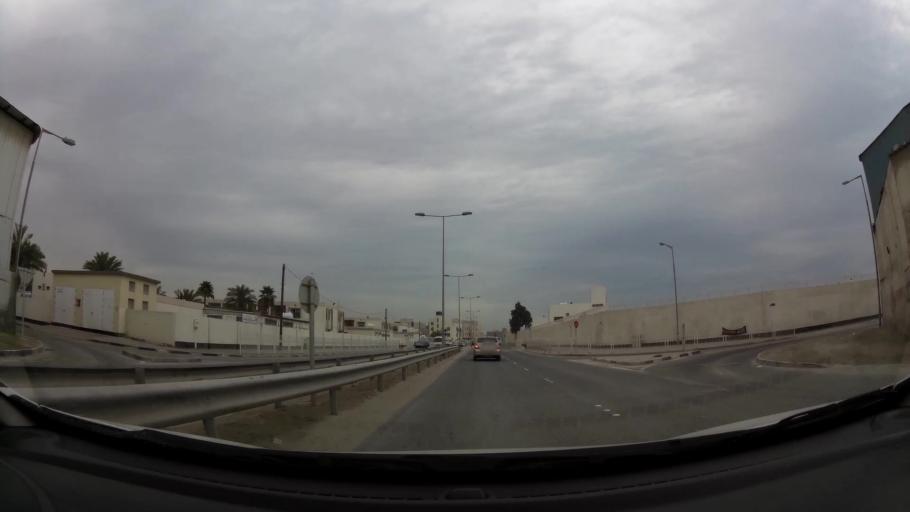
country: BH
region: Northern
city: Sitrah
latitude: 26.1546
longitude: 50.6202
